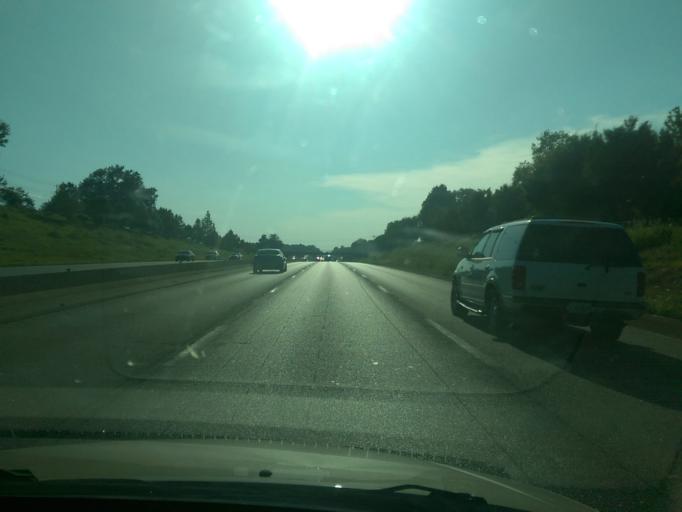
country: US
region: Missouri
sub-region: Jackson County
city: Independence
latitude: 39.0455
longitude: -94.4011
